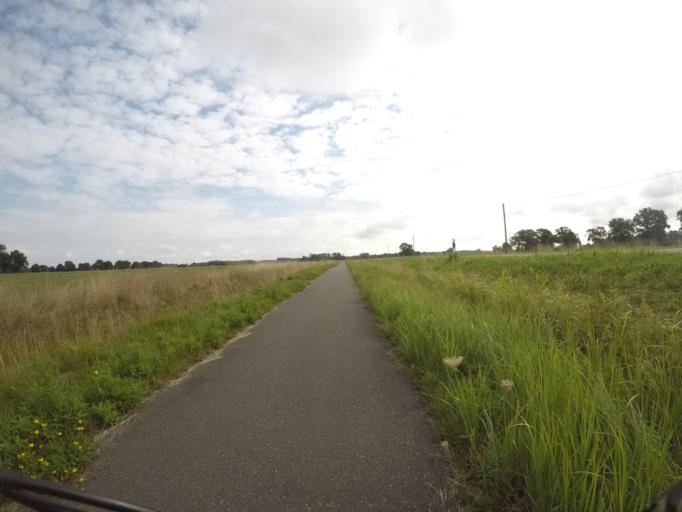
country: DE
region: Lower Saxony
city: Neu Darchau
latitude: 53.3116
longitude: 10.8748
